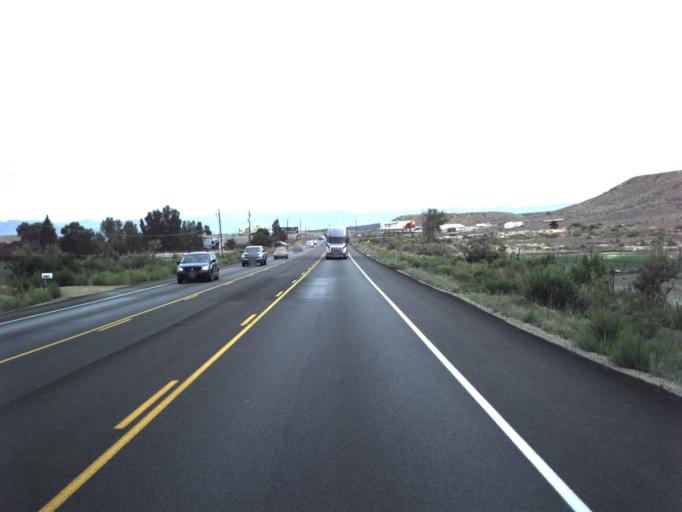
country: US
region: Utah
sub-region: Carbon County
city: Wellington
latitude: 39.5453
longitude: -110.6777
